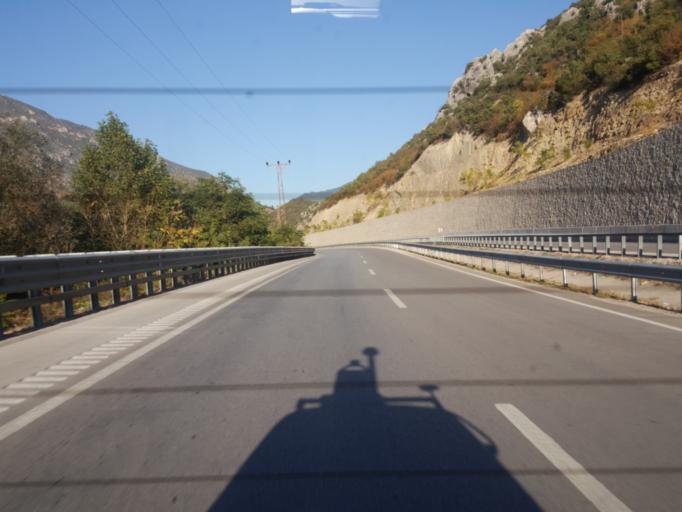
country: TR
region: Amasya
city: Amasya
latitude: 40.6845
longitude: 35.8906
